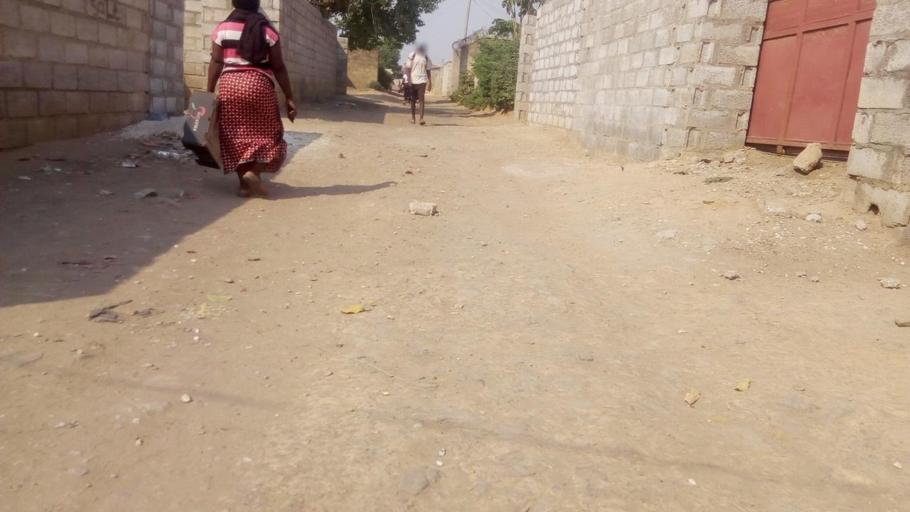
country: ZM
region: Lusaka
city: Lusaka
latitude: -15.3585
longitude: 28.2867
